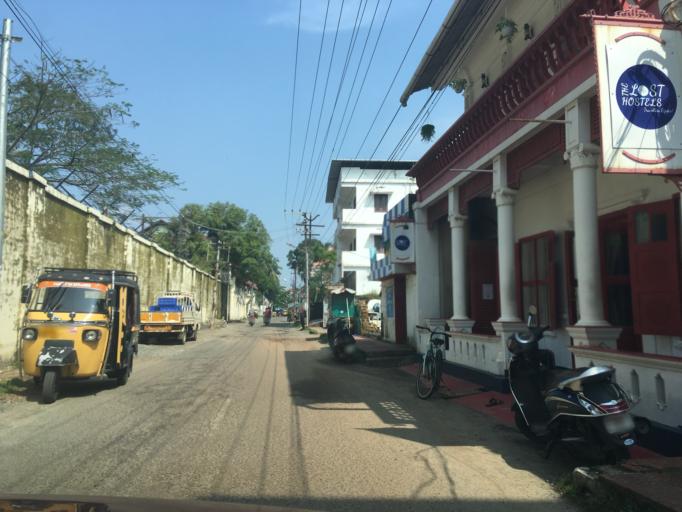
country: IN
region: Kerala
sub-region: Ernakulam
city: Cochin
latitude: 9.9685
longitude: 76.2483
